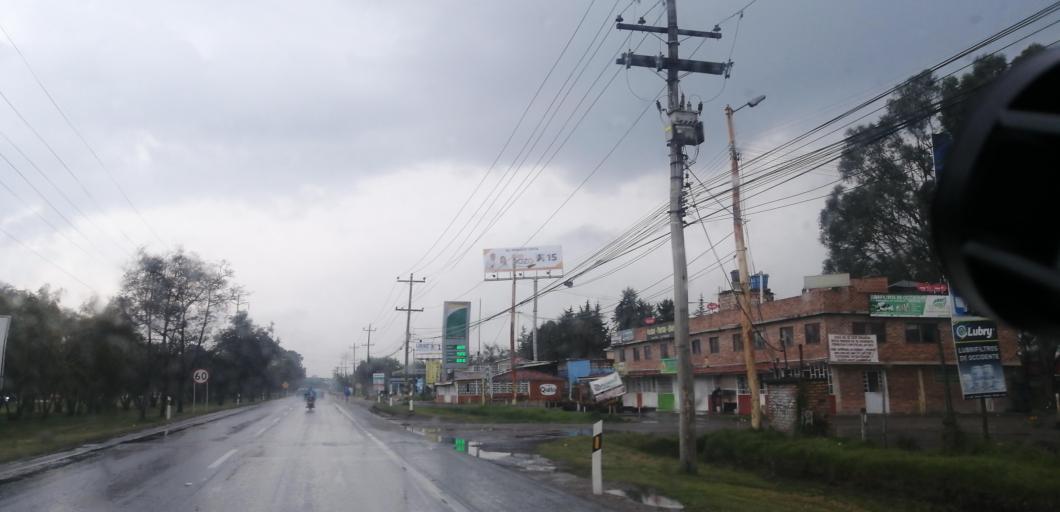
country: CO
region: Cundinamarca
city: Funza
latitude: 4.6973
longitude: -74.2118
